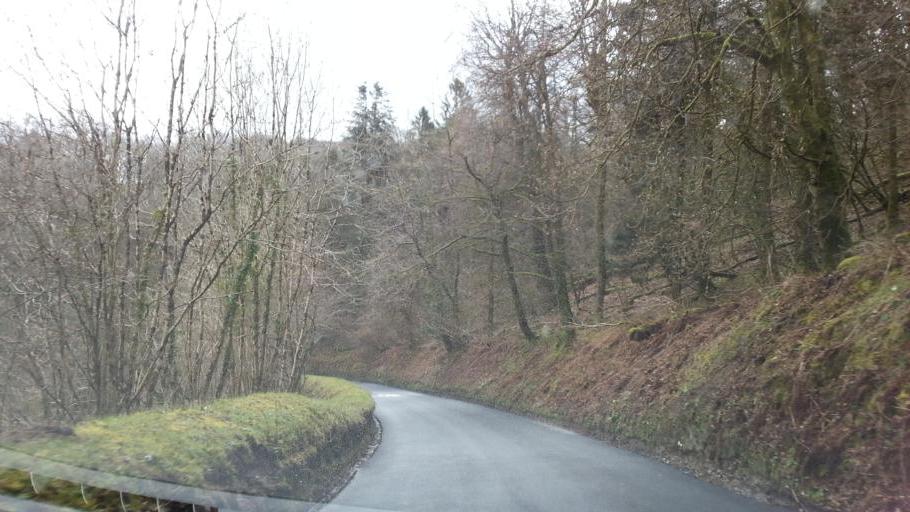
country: GB
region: England
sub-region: Devon
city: Combe Martin
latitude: 51.1436
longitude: -4.0065
